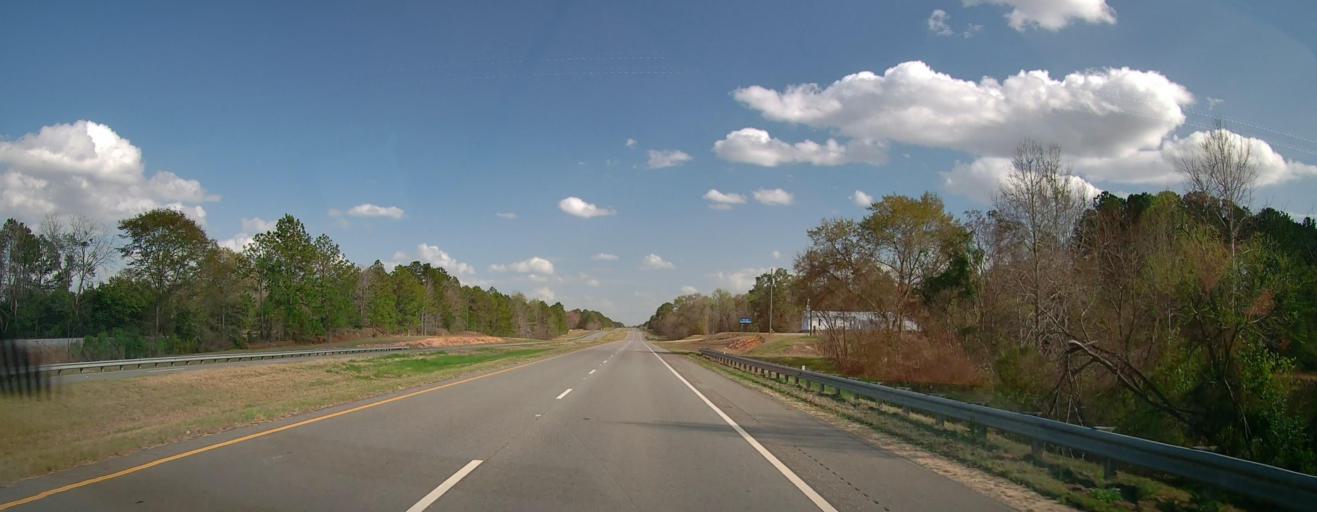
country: US
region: Georgia
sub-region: Telfair County
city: Helena
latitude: 32.1003
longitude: -82.9551
